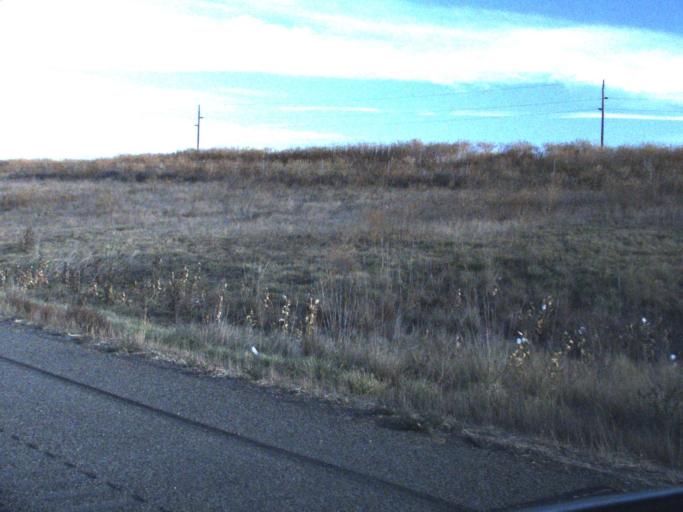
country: US
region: Washington
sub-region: Yakima County
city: Grandview
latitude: 46.2770
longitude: -119.9331
